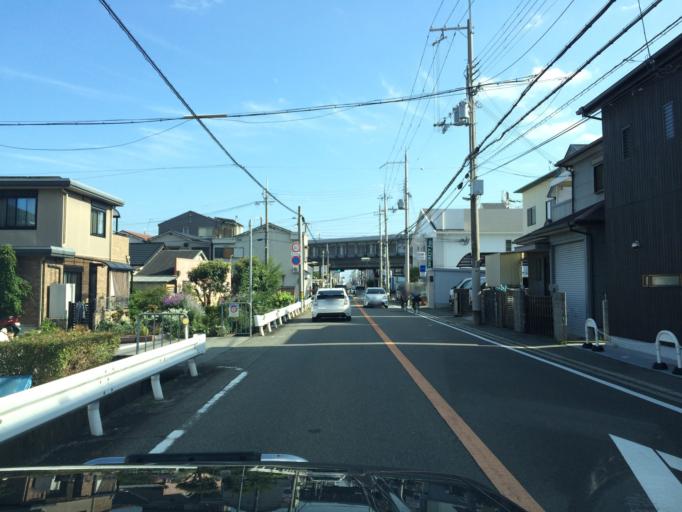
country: JP
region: Hyogo
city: Itami
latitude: 34.7696
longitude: 135.4062
